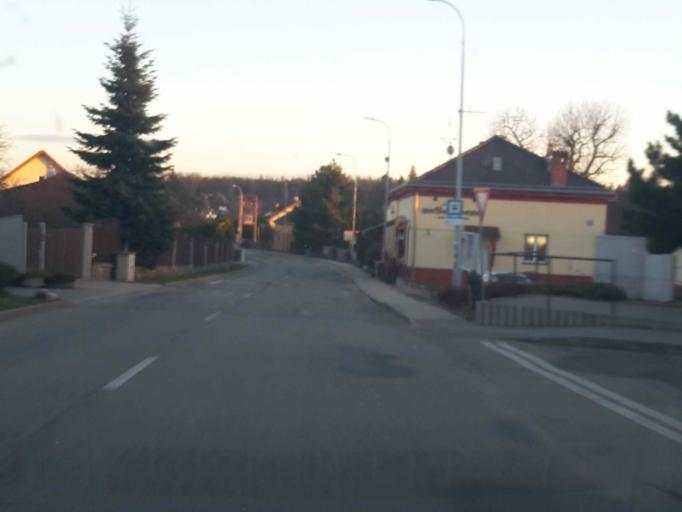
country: CZ
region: South Moravian
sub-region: Okres Blansko
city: Adamov
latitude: 49.2884
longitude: 16.6307
